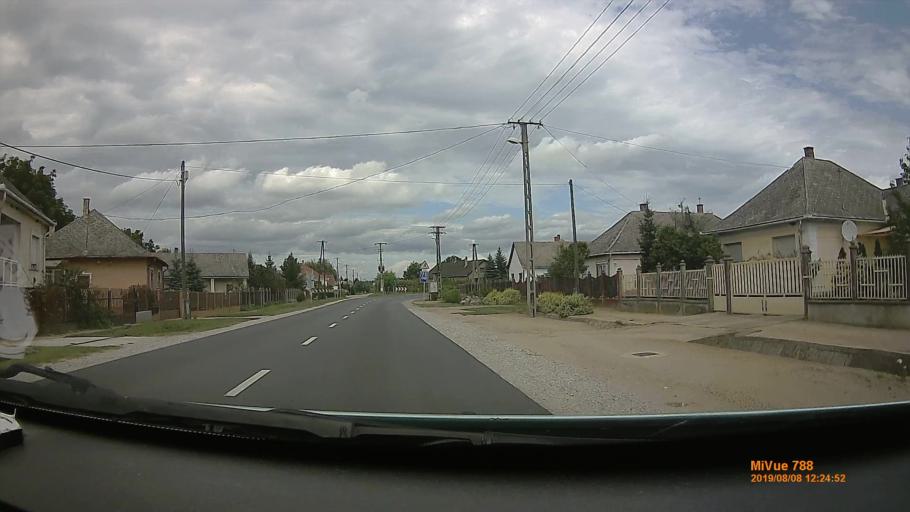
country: HU
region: Szabolcs-Szatmar-Bereg
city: Nyirbogat
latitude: 47.8076
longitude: 22.0660
